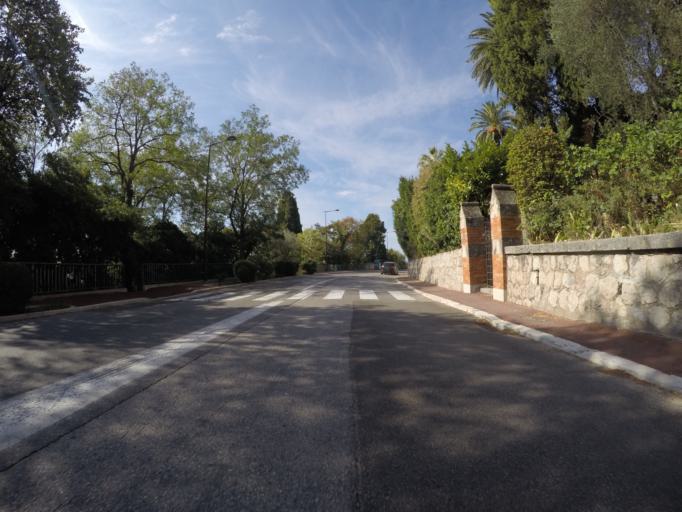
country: FR
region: Provence-Alpes-Cote d'Azur
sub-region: Departement des Alpes-Maritimes
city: Grasse
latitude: 43.6652
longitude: 6.9349
